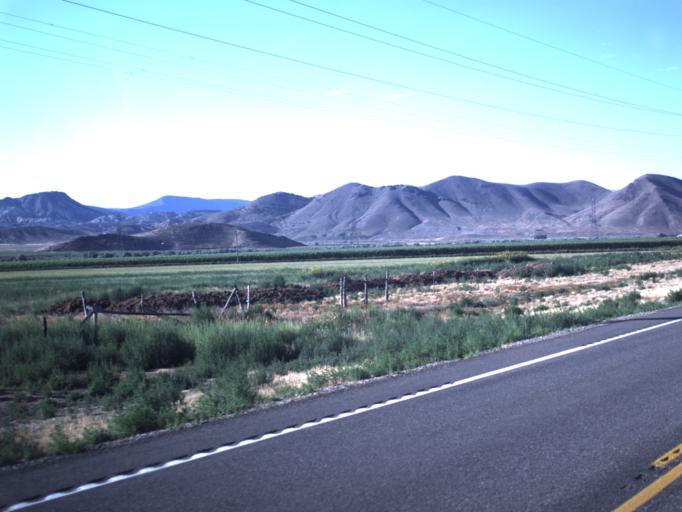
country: US
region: Utah
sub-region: Sevier County
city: Aurora
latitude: 38.9066
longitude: -111.9380
